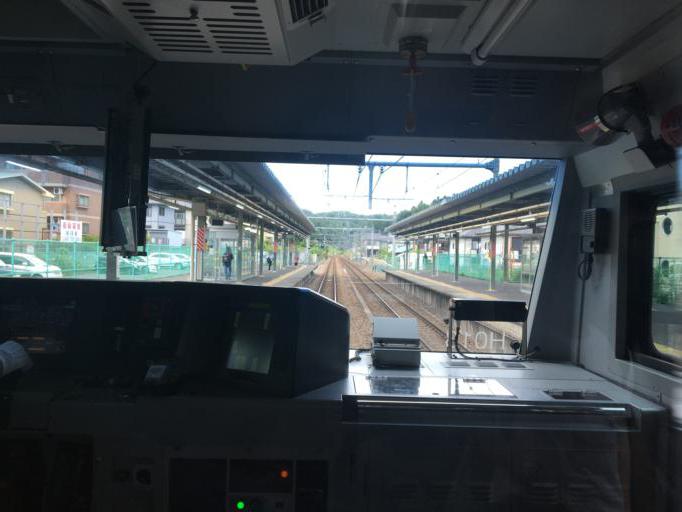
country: JP
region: Tokyo
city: Hachioji
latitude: 35.6071
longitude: 139.3316
